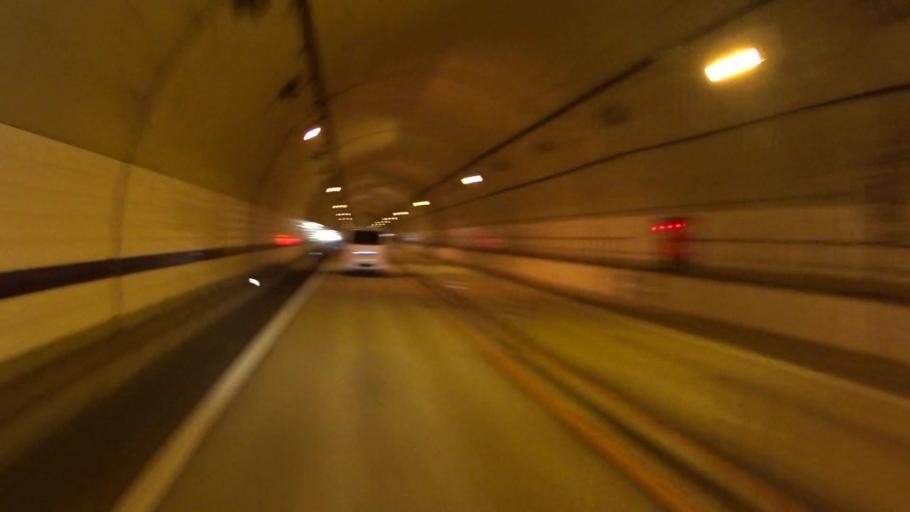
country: JP
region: Kyoto
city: Miyazu
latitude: 35.4735
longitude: 135.1757
